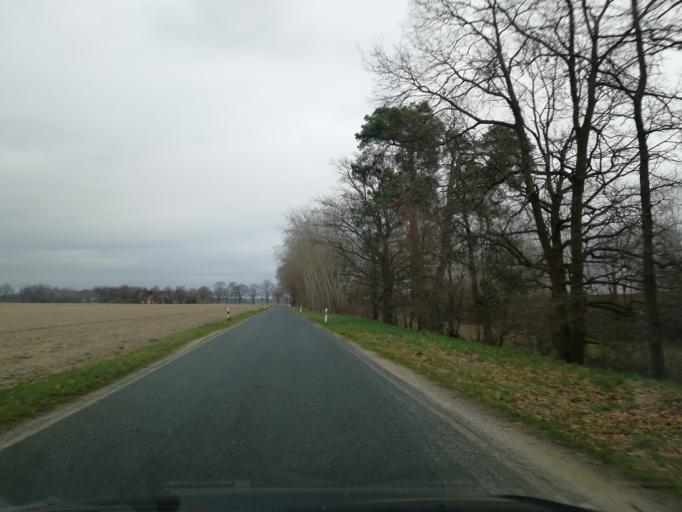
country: DE
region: Brandenburg
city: Calau
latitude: 51.7437
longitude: 13.9967
